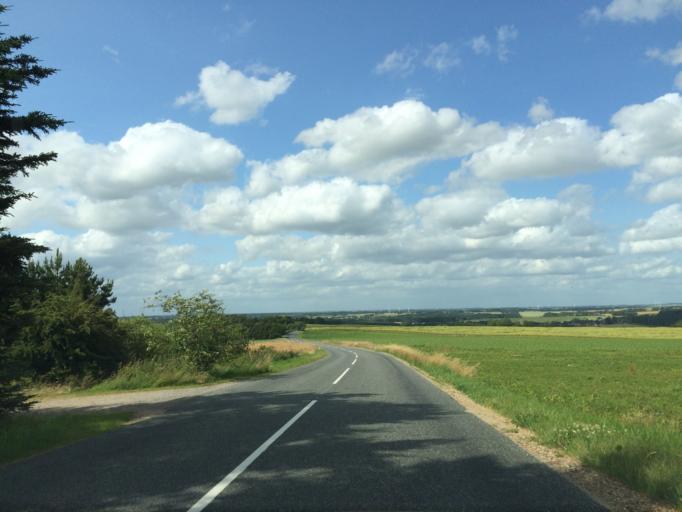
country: DK
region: Central Jutland
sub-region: Skanderborg Kommune
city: Ry
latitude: 56.2016
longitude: 9.7568
